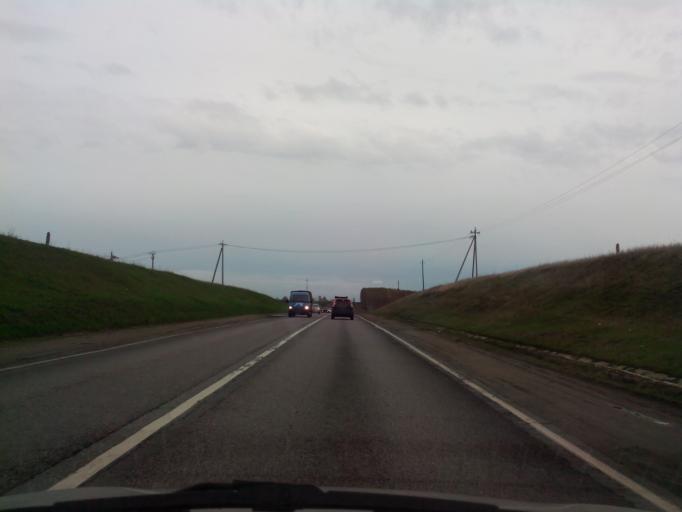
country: RU
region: Moskovskaya
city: Ozherel'ye
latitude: 54.7140
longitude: 38.2869
